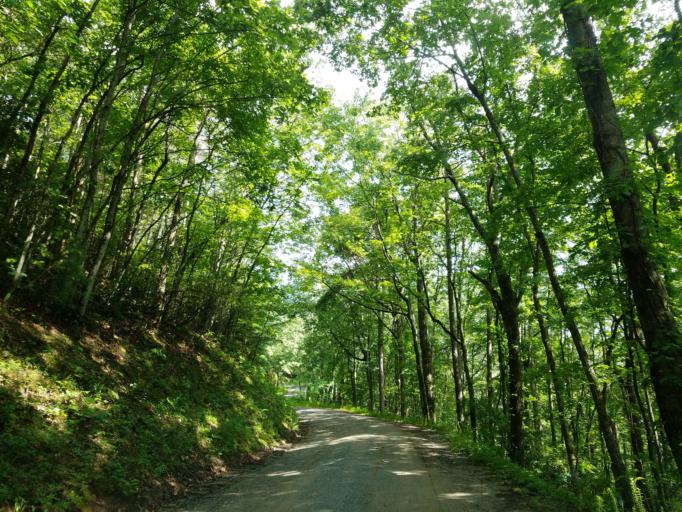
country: US
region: Georgia
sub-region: Fannin County
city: Blue Ridge
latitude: 34.6843
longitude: -84.2524
